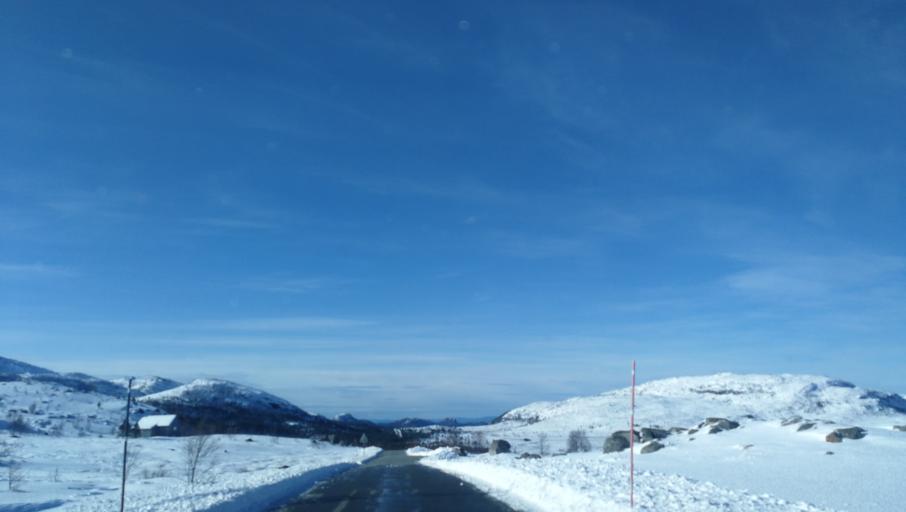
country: NO
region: Rogaland
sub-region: Hjelmeland
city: Hjelmelandsvagen
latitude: 59.1093
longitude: 6.3713
